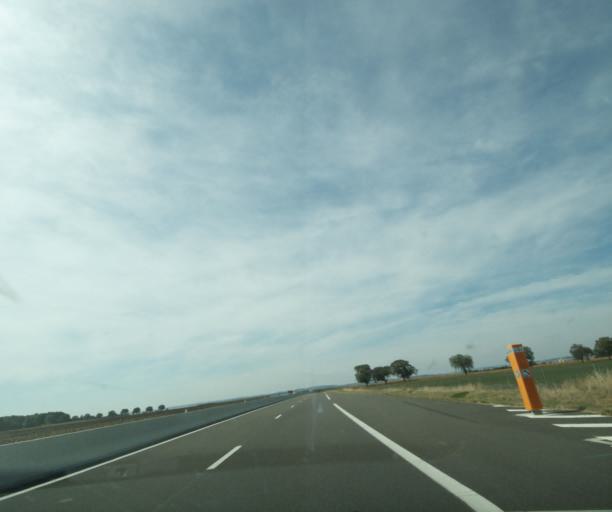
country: FR
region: Auvergne
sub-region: Departement de l'Allier
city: Brout-Vernet
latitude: 46.1159
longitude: 3.2836
